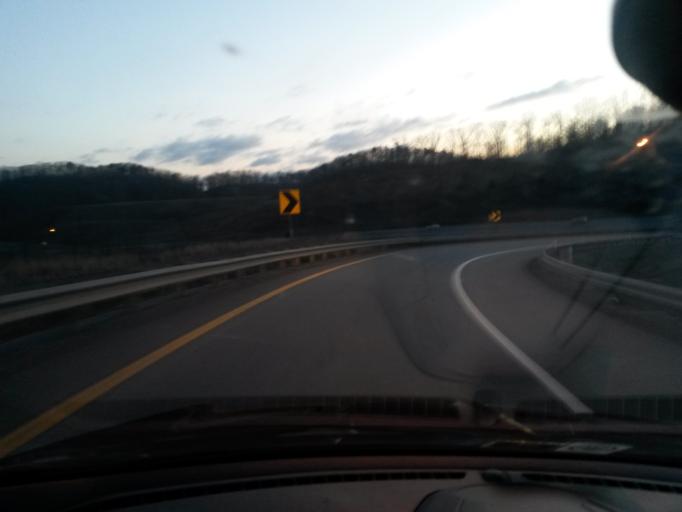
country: US
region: West Virginia
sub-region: Mercer County
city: Bluefield
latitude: 37.2757
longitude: -81.1657
